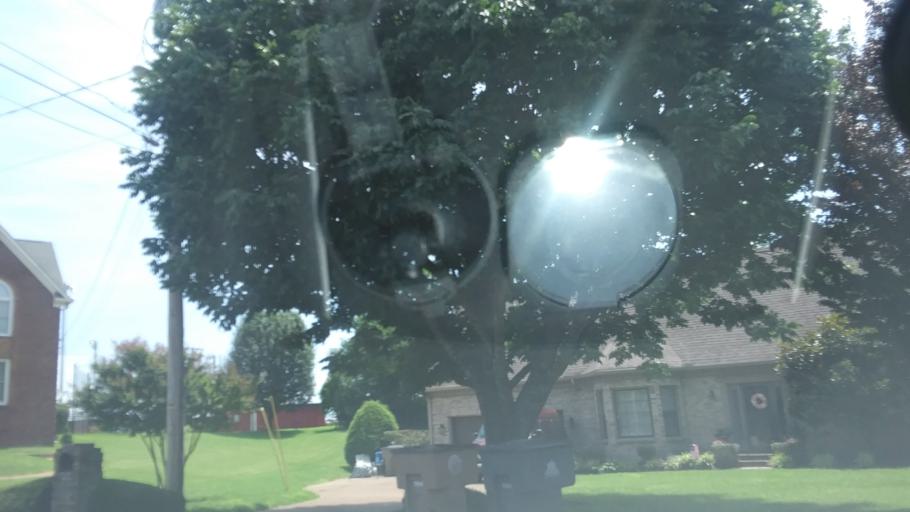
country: US
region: Tennessee
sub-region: Rutherford County
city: La Vergne
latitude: 36.0631
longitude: -86.6350
